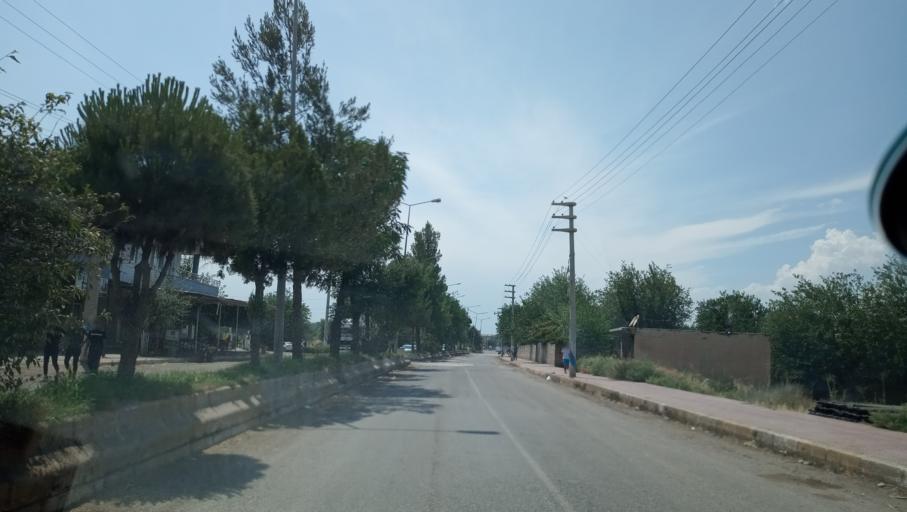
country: TR
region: Diyarbakir
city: Tepe
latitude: 37.7926
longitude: 40.7741
